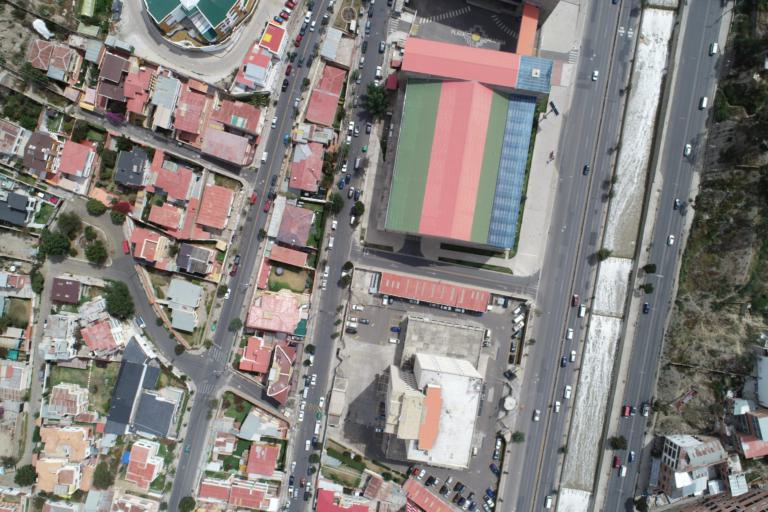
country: BO
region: La Paz
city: La Paz
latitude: -16.5383
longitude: -68.0962
